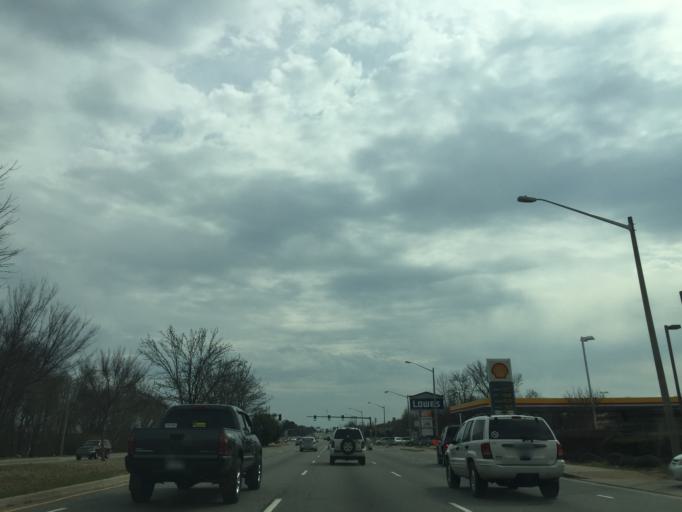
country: US
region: Virginia
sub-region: York County
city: Yorktown
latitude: 37.1248
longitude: -76.5094
